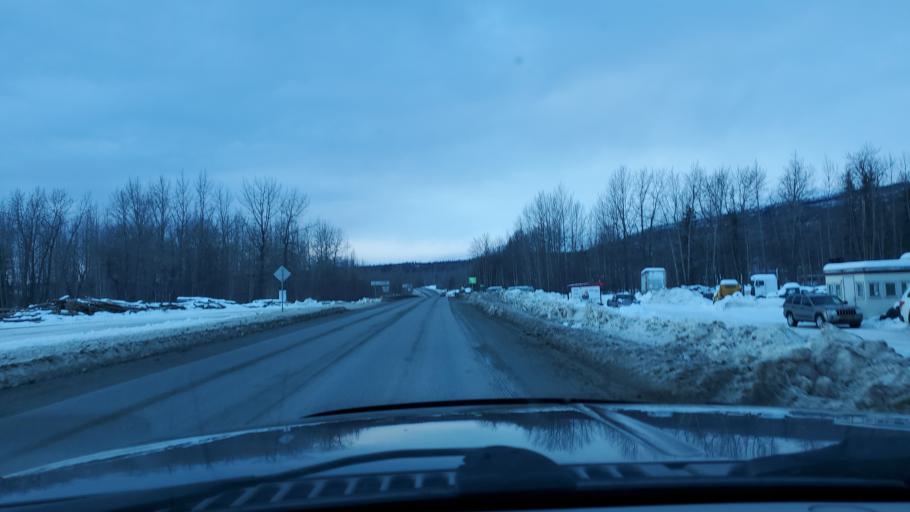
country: US
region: Alaska
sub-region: Matanuska-Susitna Borough
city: Sutton-Alpine
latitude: 61.7103
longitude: -148.8964
